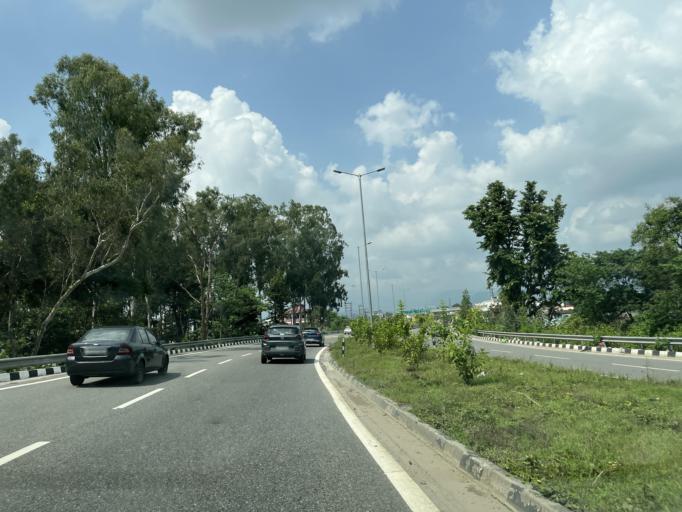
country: IN
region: Uttarakhand
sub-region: Dehradun
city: Raipur
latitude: 30.2511
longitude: 78.0933
